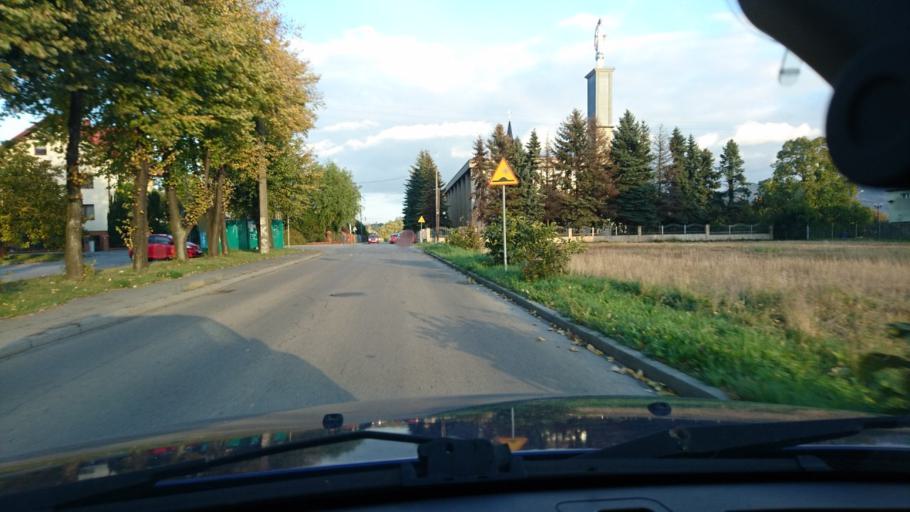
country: PL
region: Silesian Voivodeship
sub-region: Bielsko-Biala
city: Bielsko-Biala
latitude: 49.8424
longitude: 19.0614
